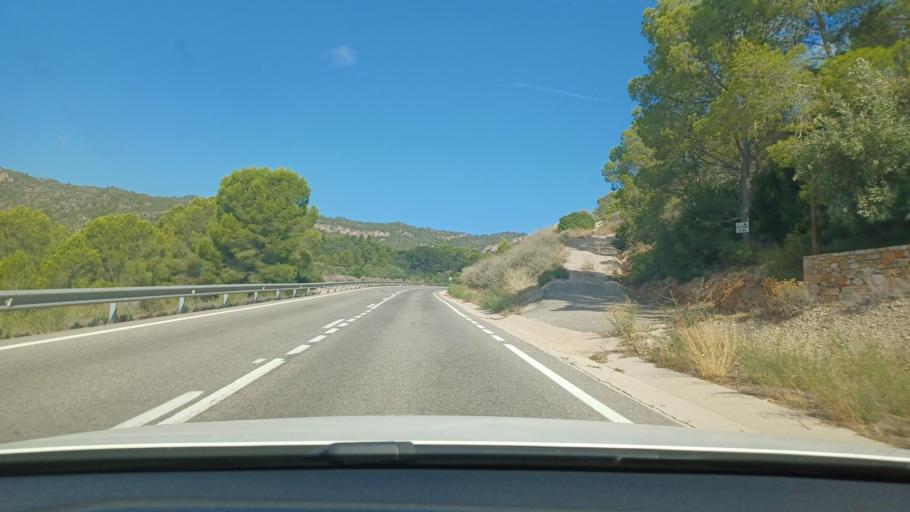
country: ES
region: Catalonia
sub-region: Provincia de Tarragona
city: Tivenys
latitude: 40.9371
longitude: 0.4697
